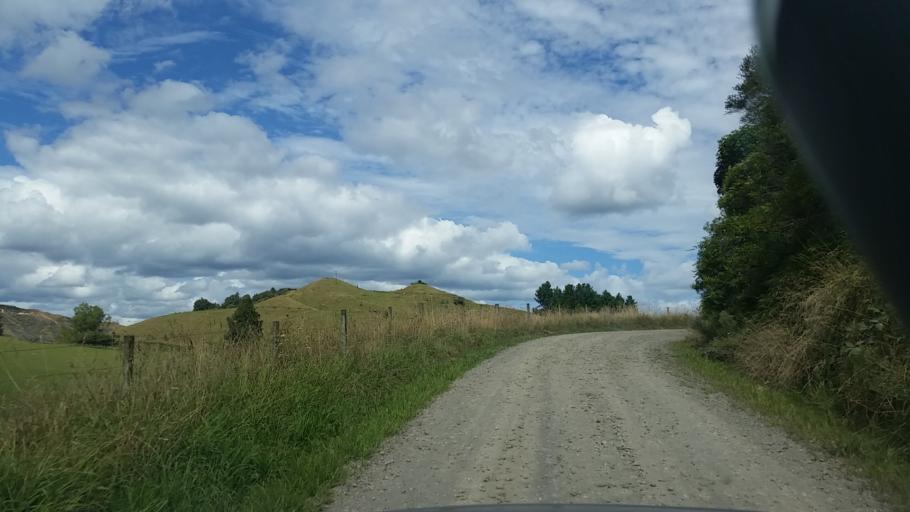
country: NZ
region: Taranaki
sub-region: South Taranaki District
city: Eltham
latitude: -39.2555
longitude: 174.5687
